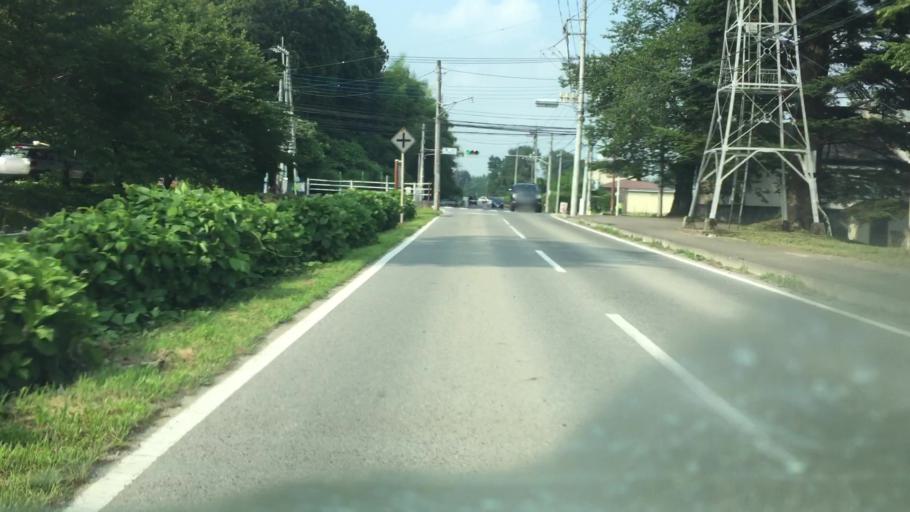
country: JP
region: Tochigi
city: Kuroiso
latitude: 36.9937
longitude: 139.9935
